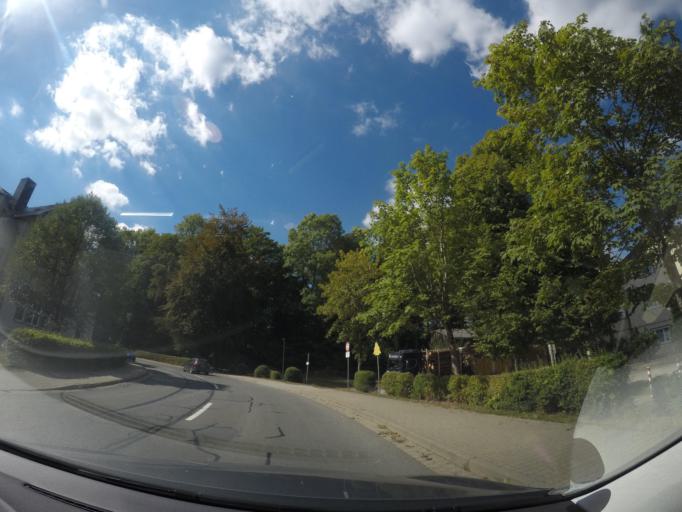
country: DE
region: Lower Saxony
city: Braunlage
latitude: 51.7443
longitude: 10.6827
